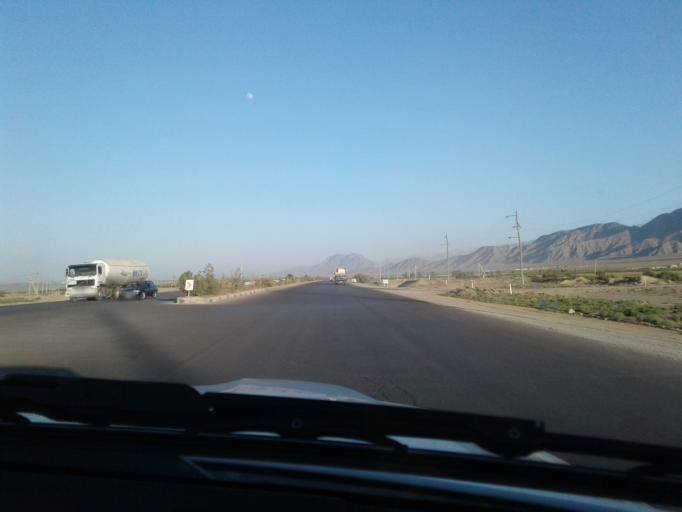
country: TM
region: Ahal
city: Baharly
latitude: 38.2246
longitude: 57.7957
